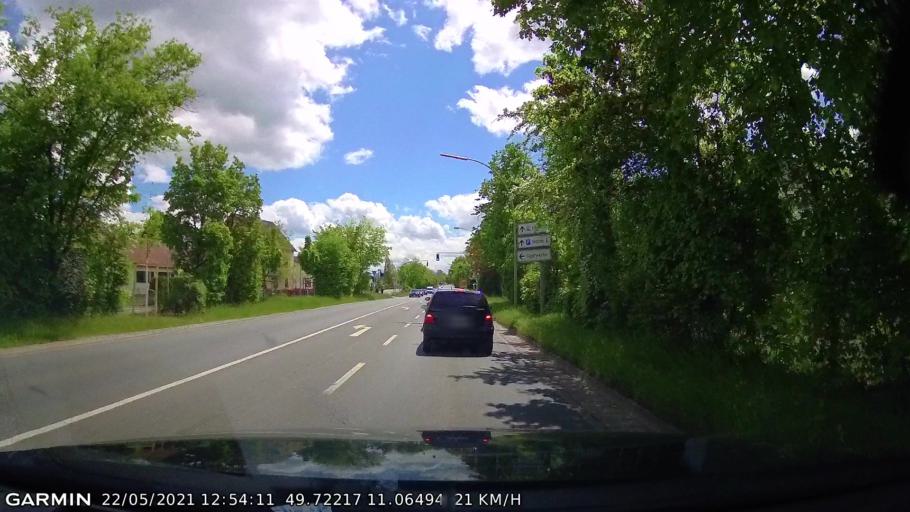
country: DE
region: Bavaria
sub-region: Upper Franconia
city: Forchheim
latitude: 49.7221
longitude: 11.0650
